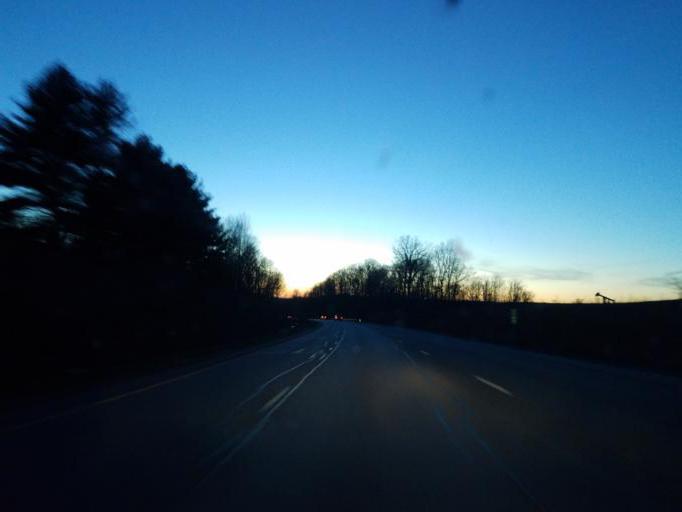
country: US
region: Ohio
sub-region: Muskingum County
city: New Concord
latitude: 39.9757
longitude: -81.8354
